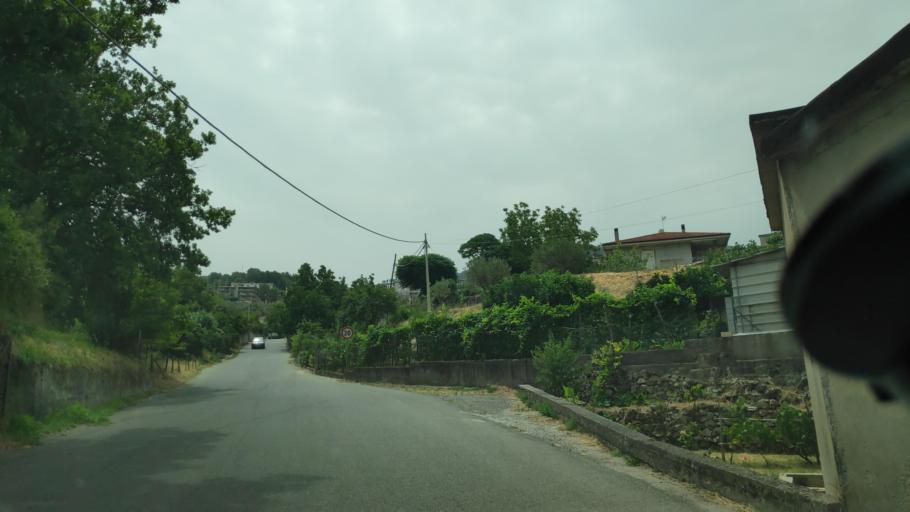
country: IT
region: Calabria
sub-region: Provincia di Catanzaro
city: Davoli
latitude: 38.6530
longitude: 16.4886
